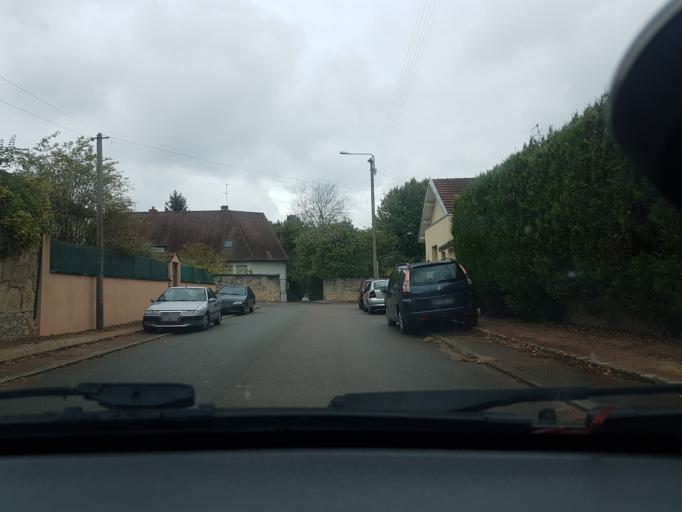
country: FR
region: Bourgogne
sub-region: Departement de la Cote-d'Or
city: Longvic
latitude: 47.3170
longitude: 5.0567
